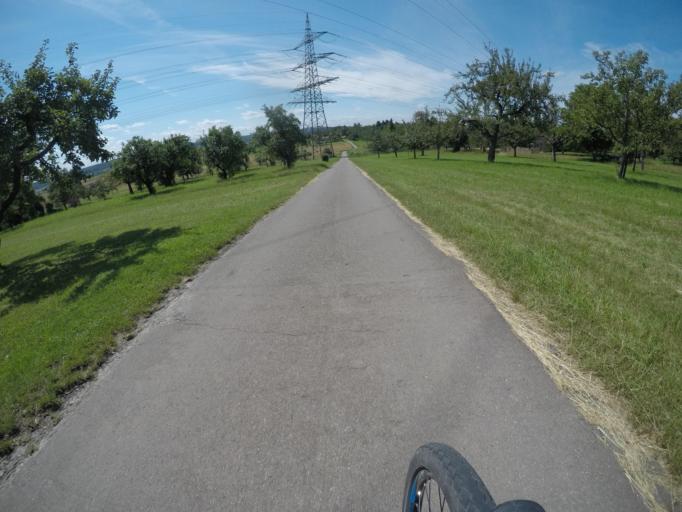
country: DE
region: Baden-Wuerttemberg
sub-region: Regierungsbezirk Stuttgart
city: Gartringen
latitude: 48.6590
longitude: 8.9070
